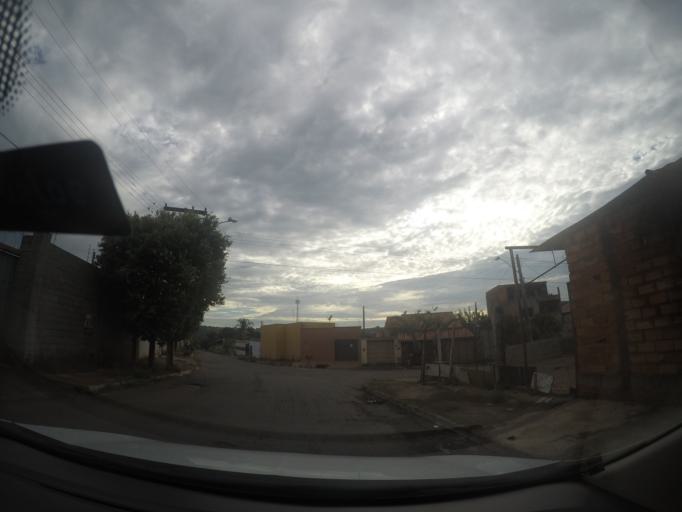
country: BR
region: Goias
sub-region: Goiania
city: Goiania
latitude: -16.6749
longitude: -49.2051
